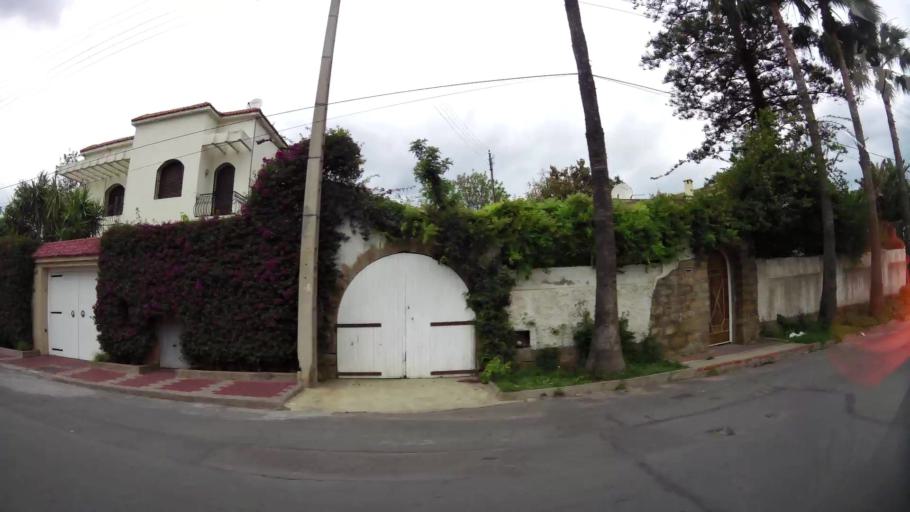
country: MA
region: Grand Casablanca
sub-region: Casablanca
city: Casablanca
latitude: 33.5634
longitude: -7.6426
